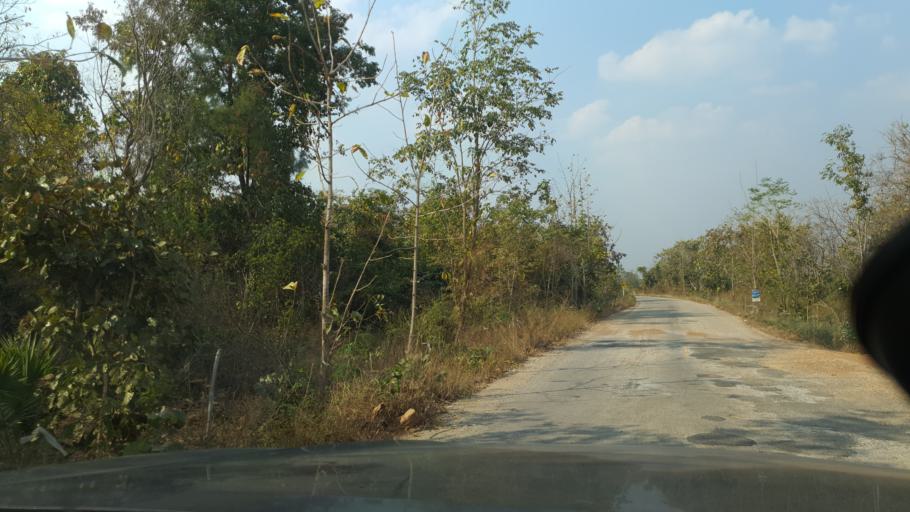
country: TH
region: Sukhothai
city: Ban Dan Lan Hoi
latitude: 17.0186
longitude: 99.5578
